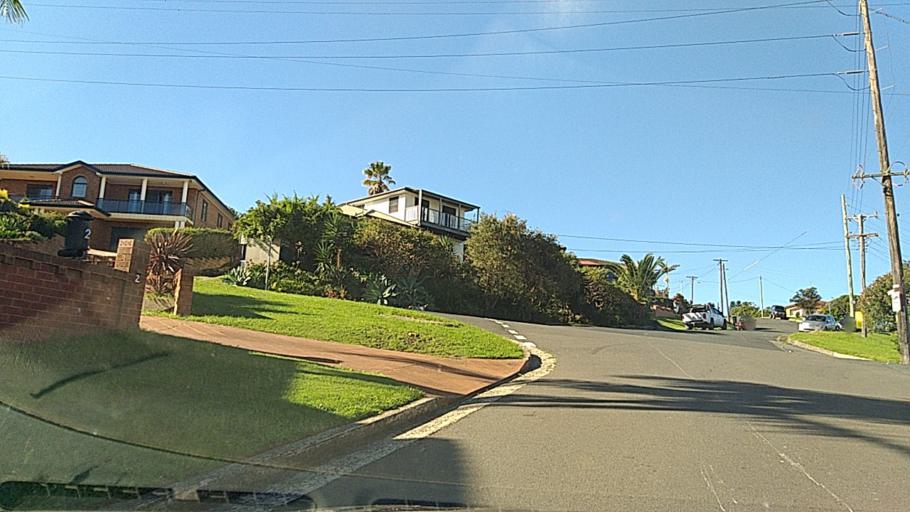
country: AU
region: New South Wales
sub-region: Wollongong
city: Port Kembla
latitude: -34.4819
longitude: 150.8886
